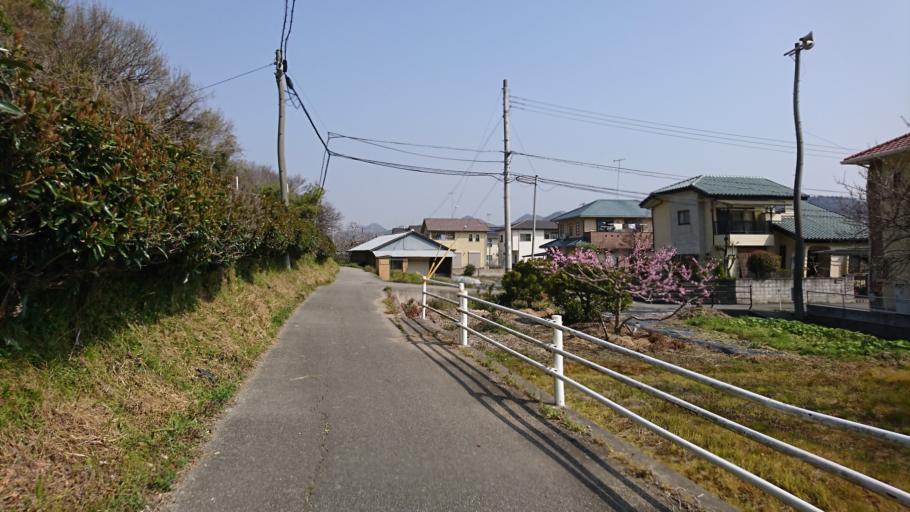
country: JP
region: Hyogo
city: Shirahamacho-usazakiminami
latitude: 34.7886
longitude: 134.7647
